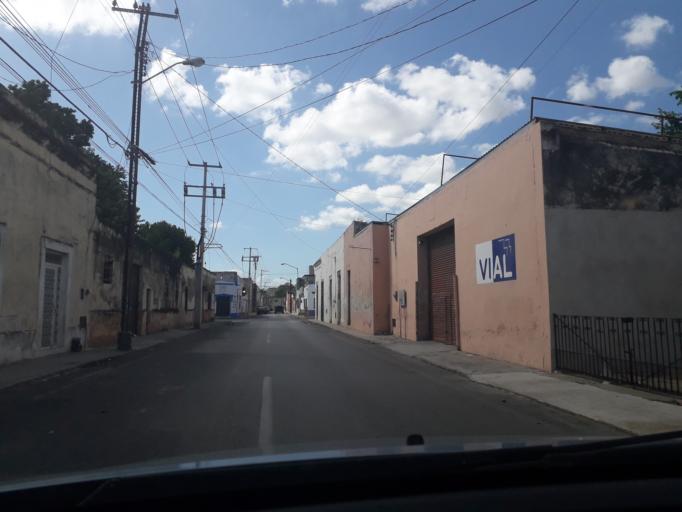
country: MX
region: Yucatan
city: Merida
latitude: 20.9603
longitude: -89.6267
